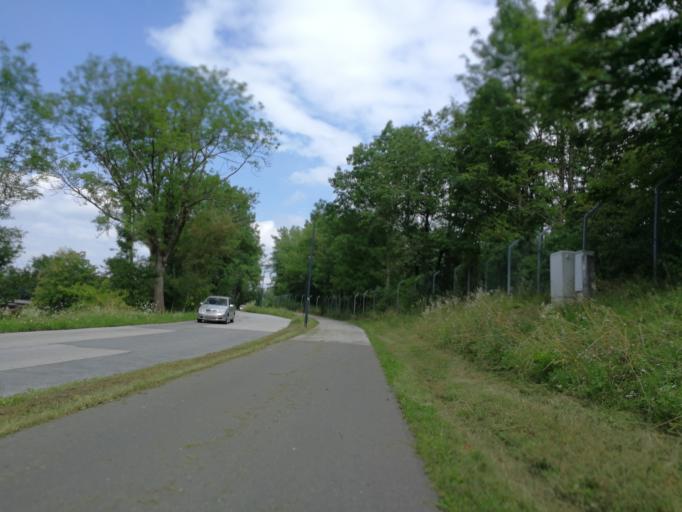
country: DE
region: Bavaria
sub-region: Upper Bavaria
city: Ainring
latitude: 47.7929
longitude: 12.9697
